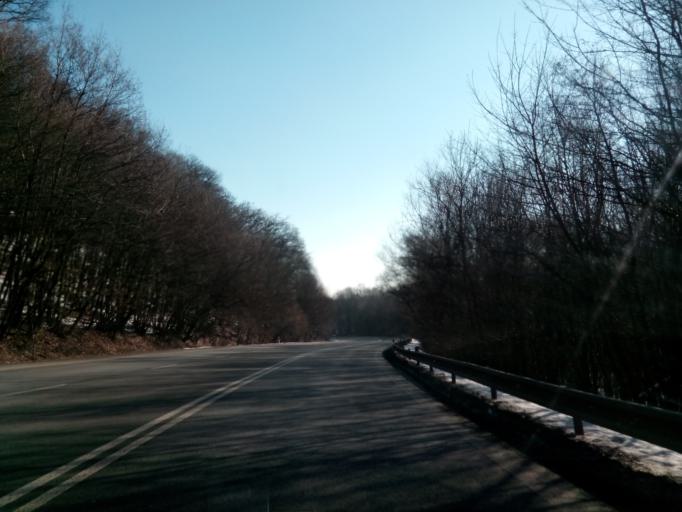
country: SK
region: Kosicky
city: Secovce
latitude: 48.7352
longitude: 21.5593
